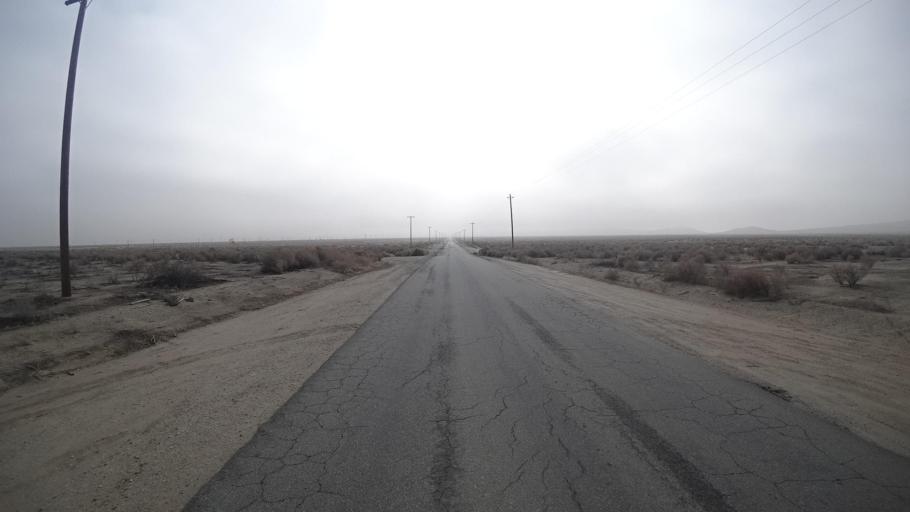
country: US
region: California
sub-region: Kern County
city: Ford City
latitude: 35.2075
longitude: -119.4291
